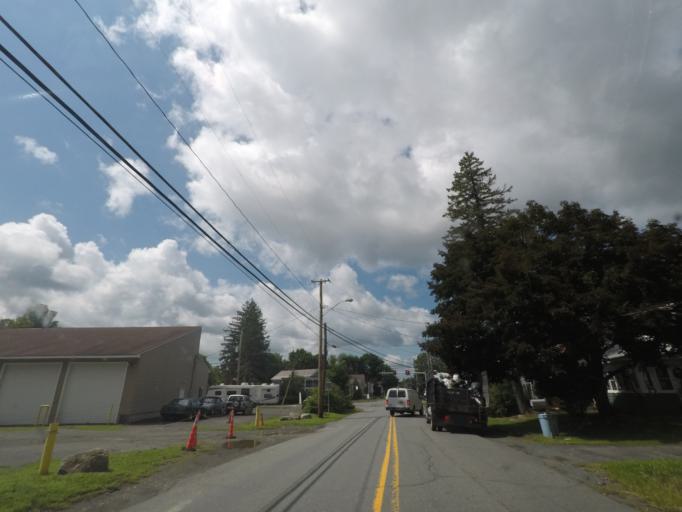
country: US
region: New York
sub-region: Rensselaer County
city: Averill Park
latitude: 42.6378
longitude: -73.5399
